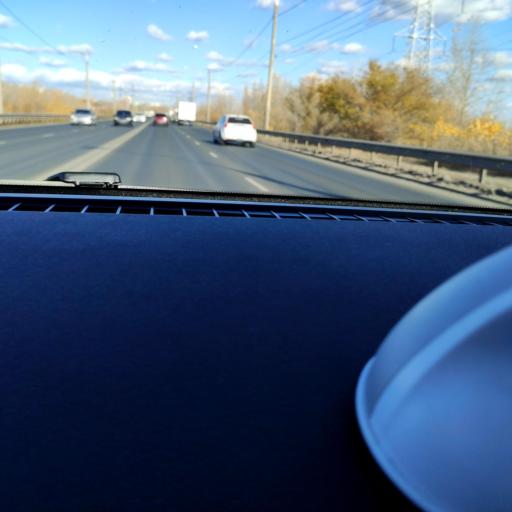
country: RU
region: Samara
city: Samara
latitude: 53.1599
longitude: 50.1933
